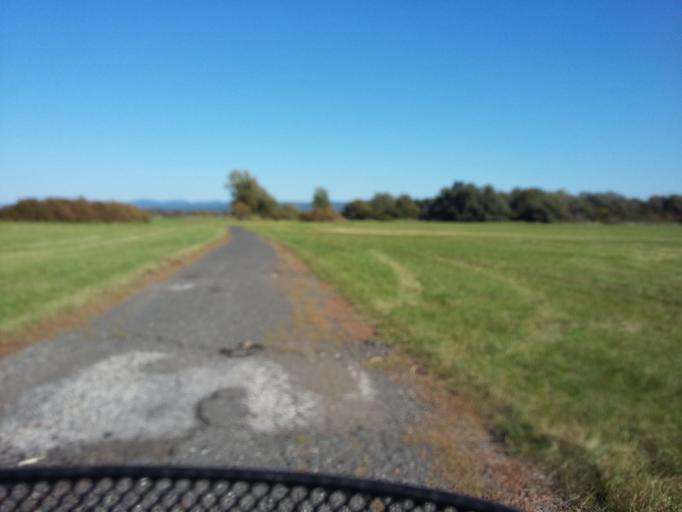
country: AT
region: Lower Austria
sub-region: Politischer Bezirk Ganserndorf
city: Marchegg
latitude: 48.2733
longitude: 16.9388
